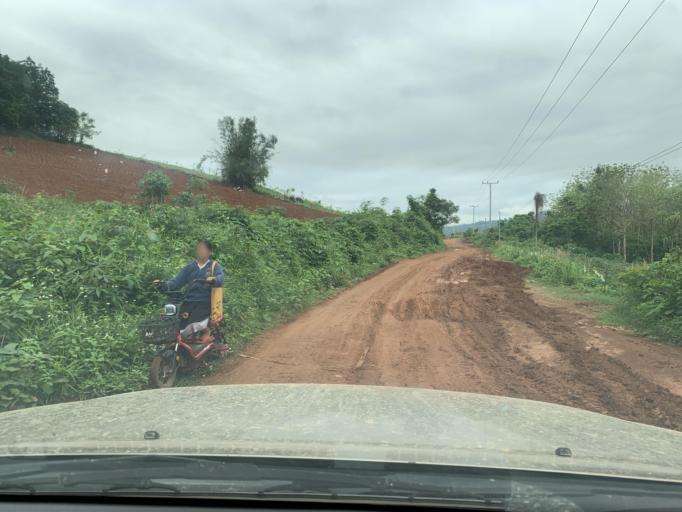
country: TH
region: Nan
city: Mae Charim
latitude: 18.4155
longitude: 101.4441
